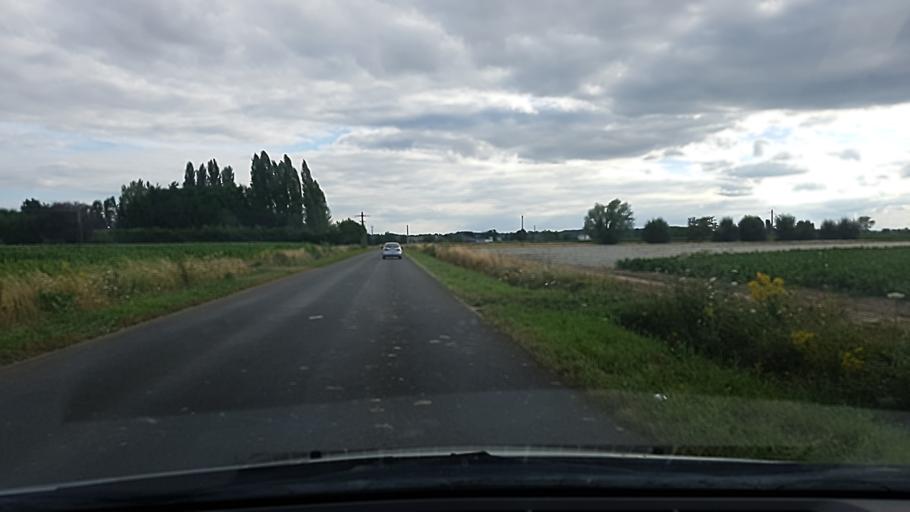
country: FR
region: Pays de la Loire
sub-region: Departement de Maine-et-Loire
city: Saint-Mathurin-sur-Loire
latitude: 47.4225
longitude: -0.3067
